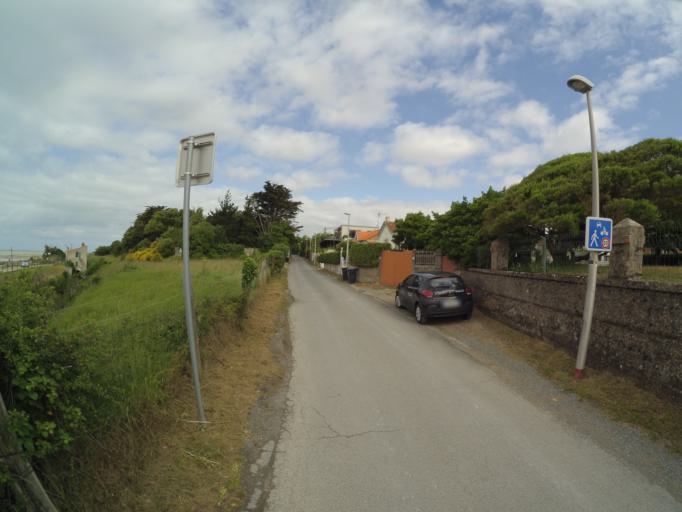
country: FR
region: Poitou-Charentes
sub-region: Departement de la Charente-Maritime
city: Angoulins
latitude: 46.0951
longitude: -1.1014
